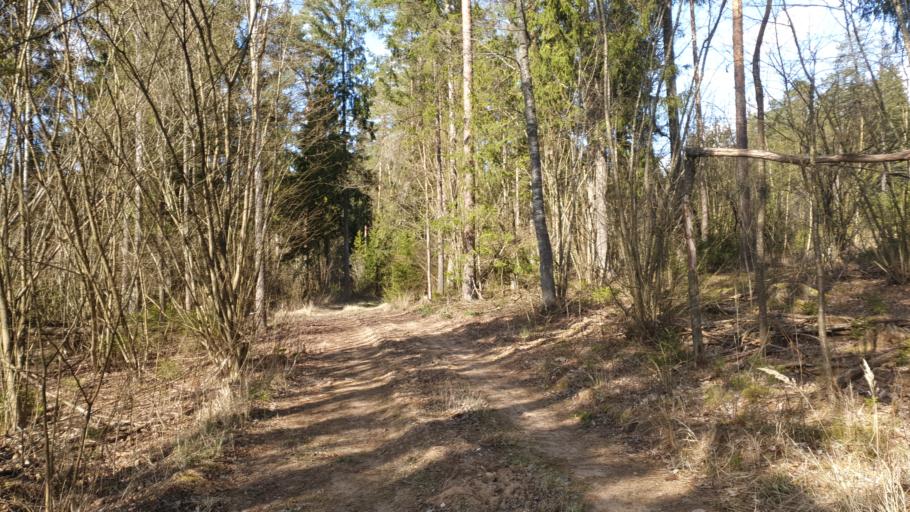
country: LT
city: Aukstadvaris
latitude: 54.4953
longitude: 24.6509
